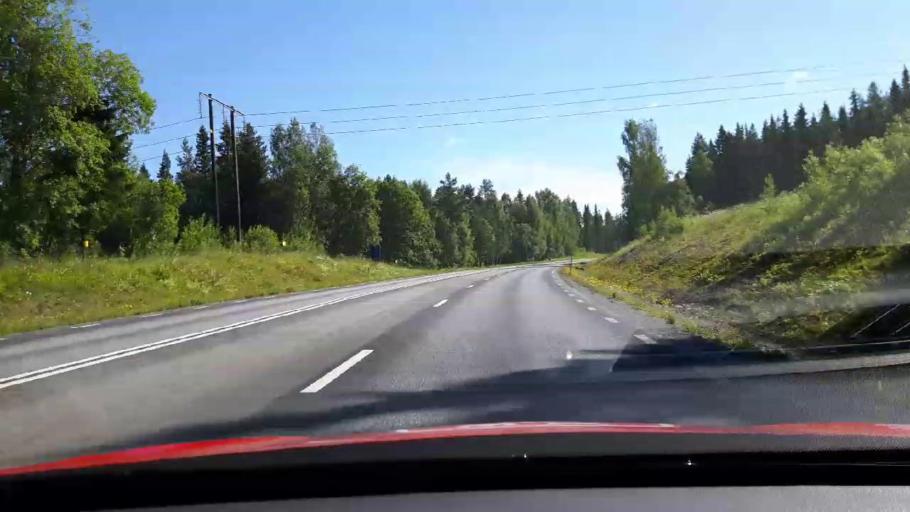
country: SE
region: Jaemtland
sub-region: OEstersunds Kommun
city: Ostersund
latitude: 63.2079
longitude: 14.6868
